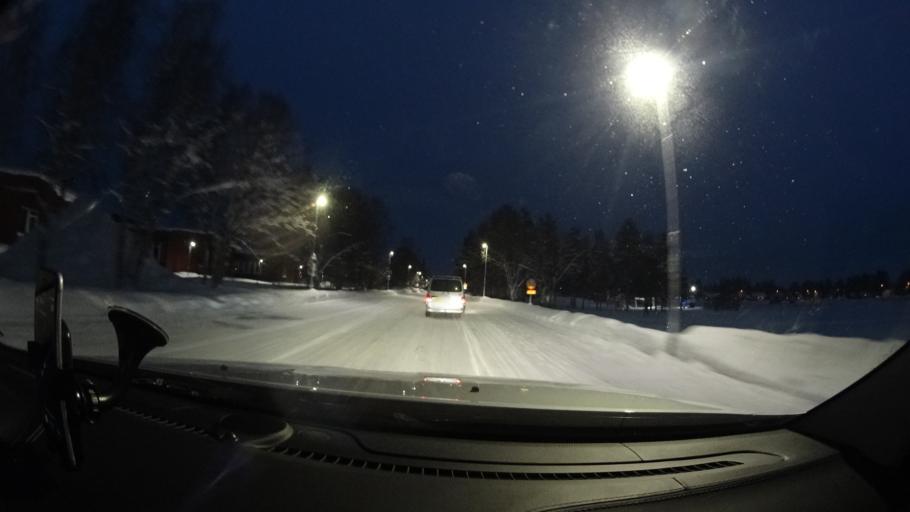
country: SE
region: Norrbotten
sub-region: Gallivare Kommun
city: Malmberget
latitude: 67.6776
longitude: 21.6381
